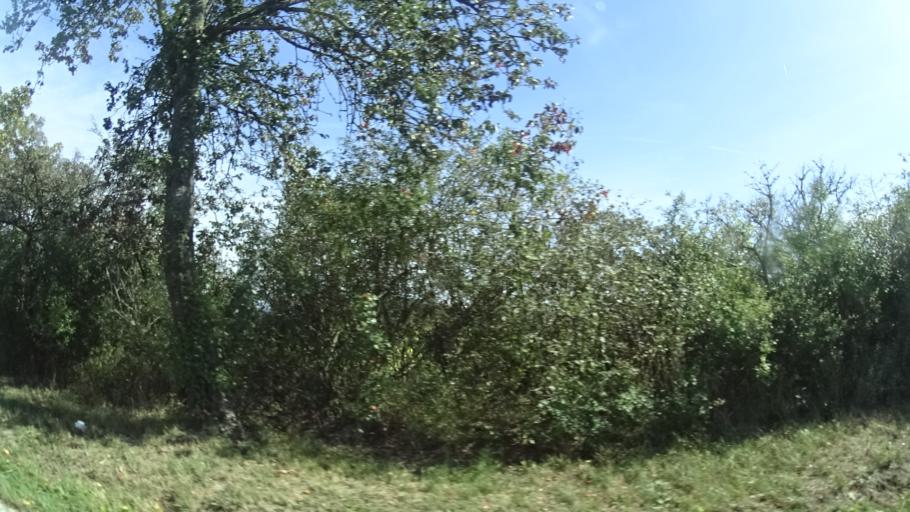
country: DE
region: Thuringia
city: Rottenbach
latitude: 50.7353
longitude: 11.2146
